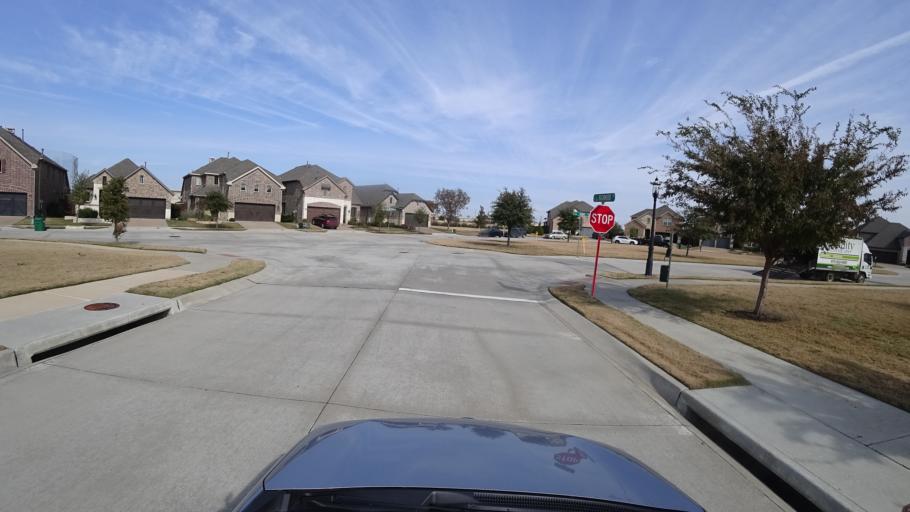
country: US
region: Texas
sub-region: Denton County
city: The Colony
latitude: 33.0674
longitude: -96.8793
